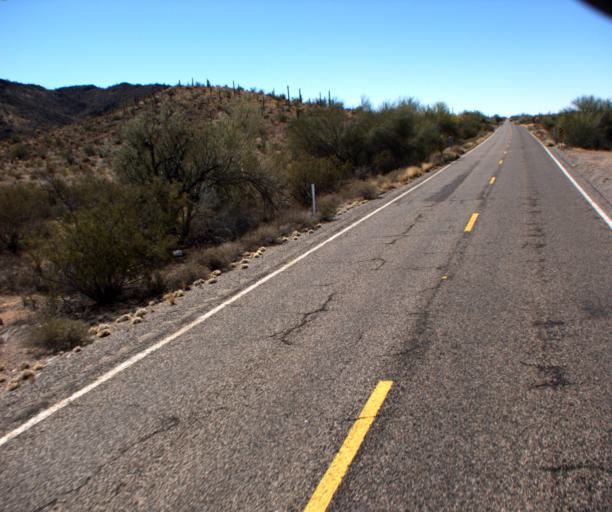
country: US
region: Arizona
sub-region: Pima County
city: Ajo
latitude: 32.2182
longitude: -112.7573
